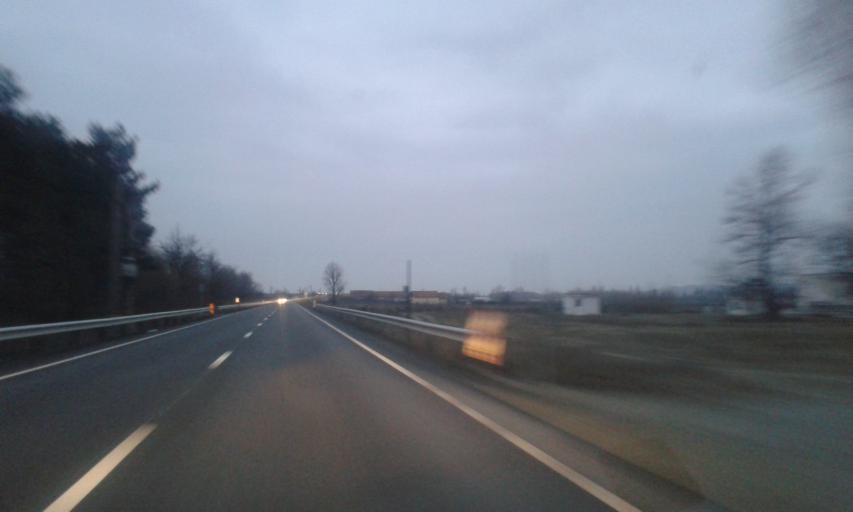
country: RO
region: Gorj
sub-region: Comuna Turcinesti
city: Turcinesti
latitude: 45.1113
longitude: 23.3427
